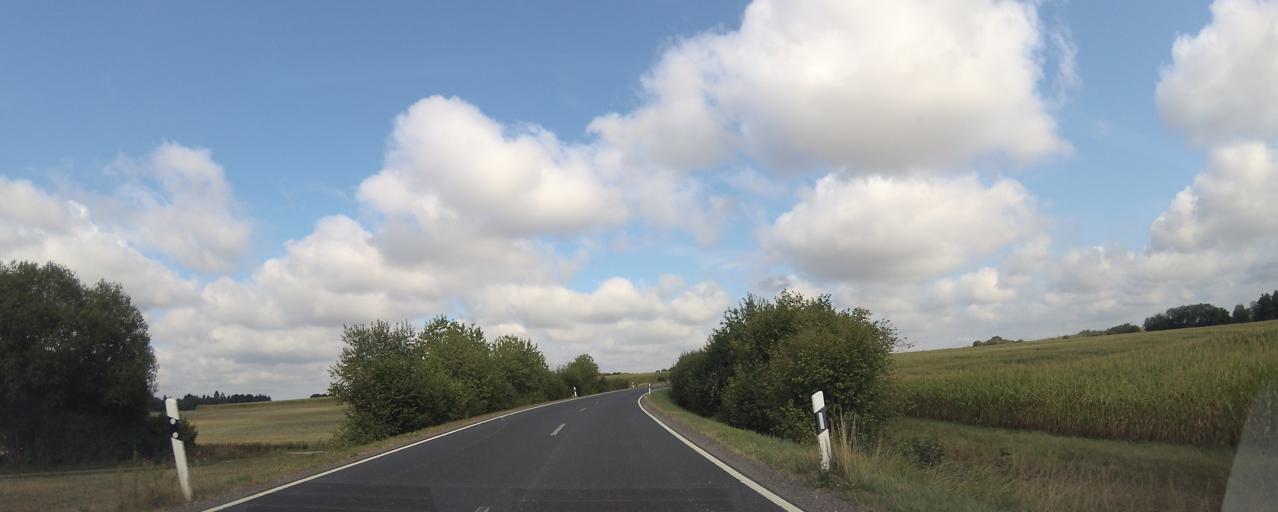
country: DE
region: Rheinland-Pfalz
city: Herforst
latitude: 49.9515
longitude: 6.6862
